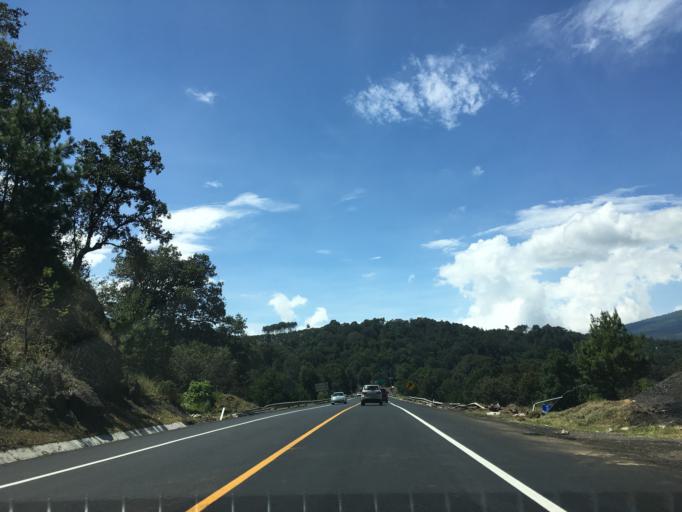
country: MX
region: Michoacan
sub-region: Patzcuaro
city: Santa Maria Huiramangaro (San Juan Tumbio)
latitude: 19.4851
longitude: -101.7243
